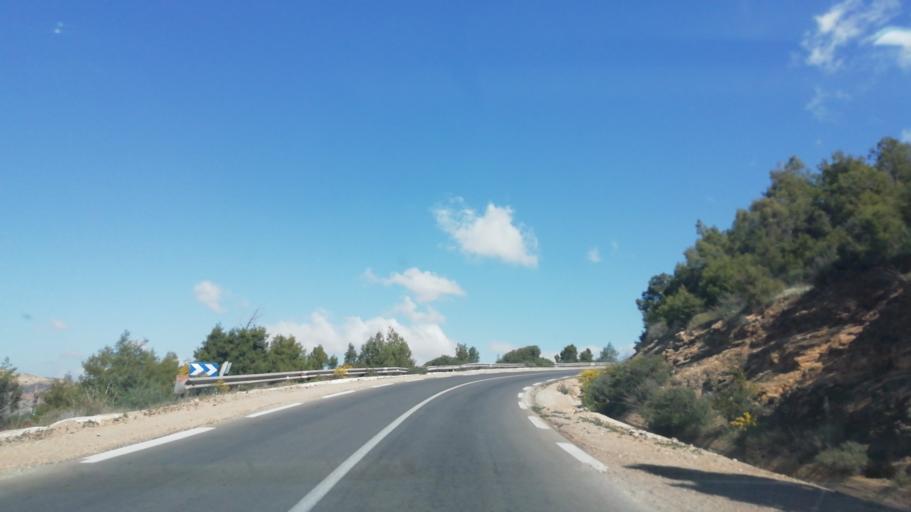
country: DZ
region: Mascara
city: Mascara
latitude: 35.4891
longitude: 0.1431
